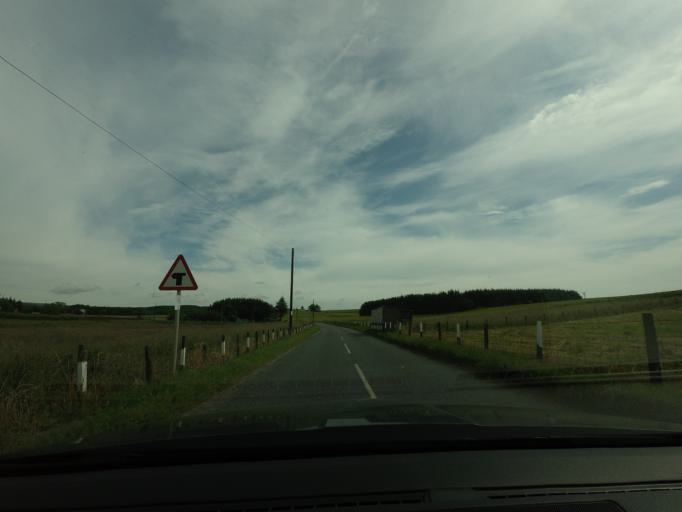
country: GB
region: Scotland
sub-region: Aberdeenshire
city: Turriff
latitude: 57.5708
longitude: -2.2960
